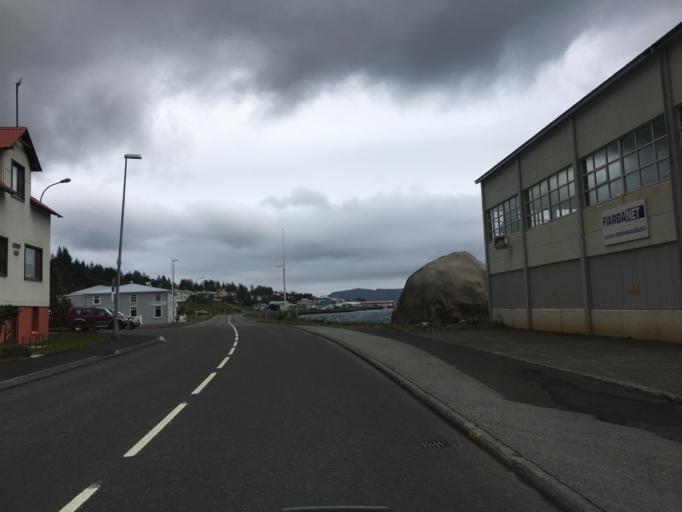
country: IS
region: East
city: Neskaupstadur
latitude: 65.1474
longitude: -13.7048
